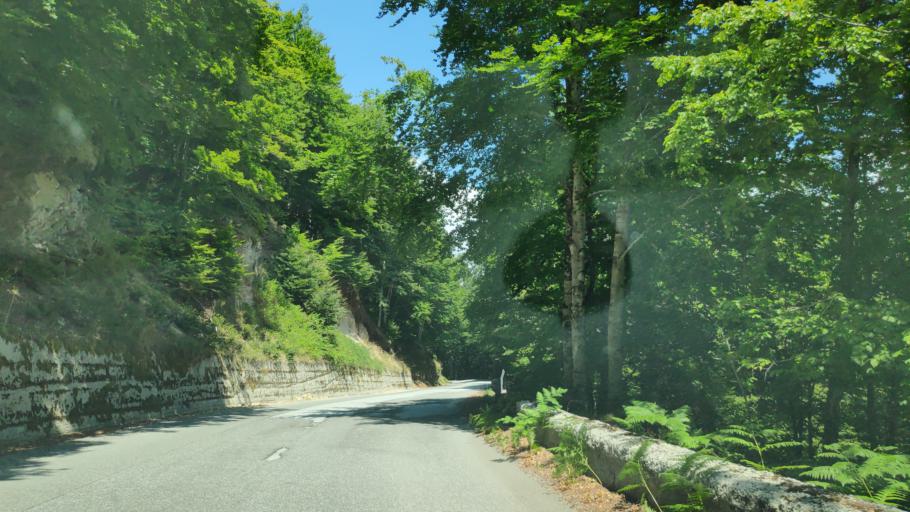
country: IT
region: Calabria
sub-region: Provincia di Vibo-Valentia
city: Mongiana
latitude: 38.5100
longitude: 16.3520
